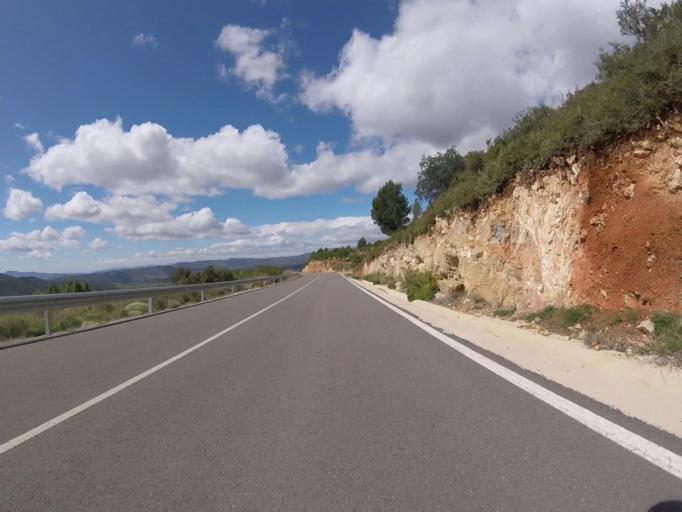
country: ES
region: Valencia
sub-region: Provincia de Castello
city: Culla
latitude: 40.2949
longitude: -0.1187
